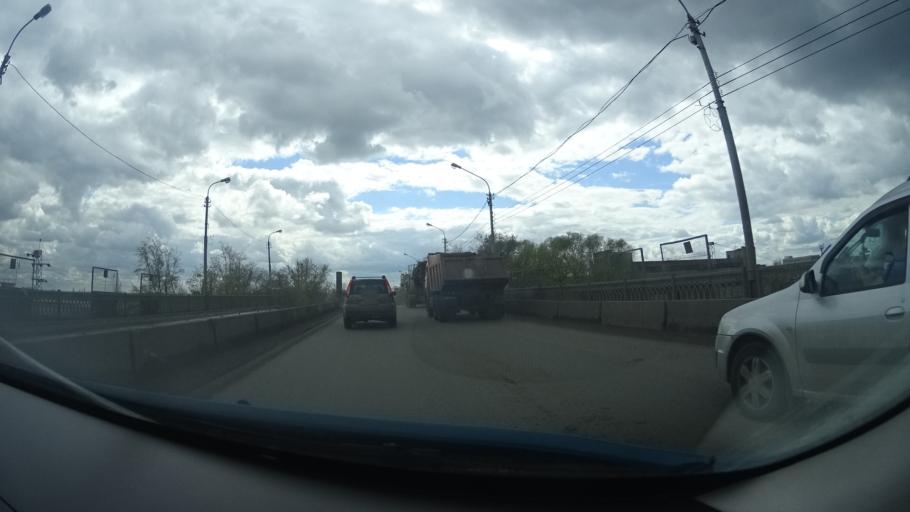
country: RU
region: Bashkortostan
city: Ufa
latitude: 54.8091
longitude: 56.0860
